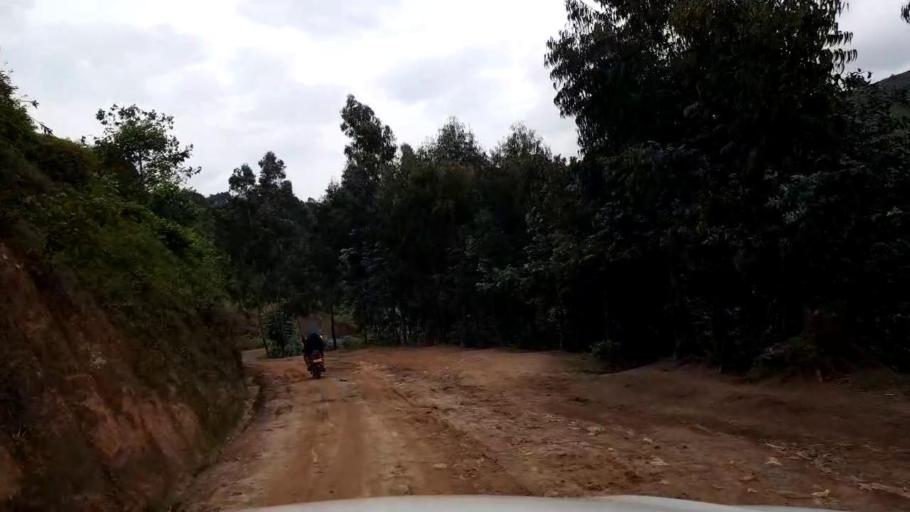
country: RW
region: Western Province
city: Kibuye
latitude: -1.9534
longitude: 29.4223
